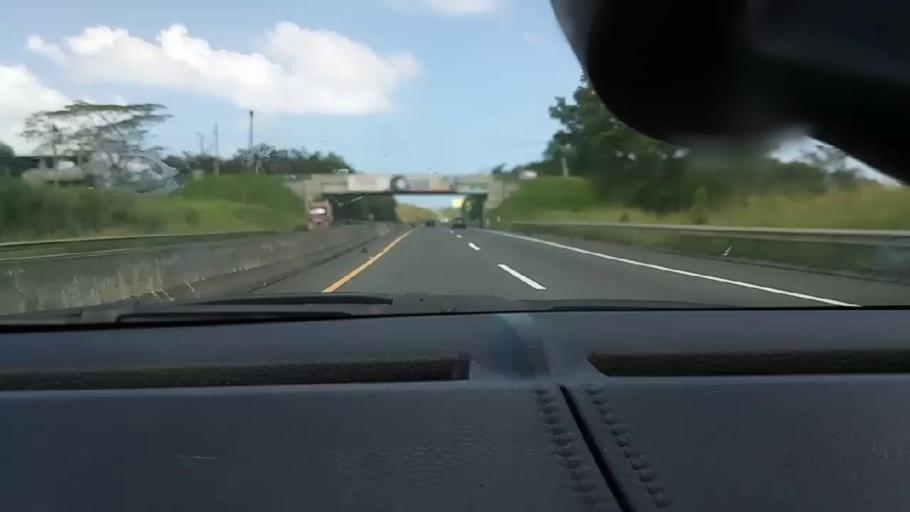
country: PA
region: Colon
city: Las Margaritas
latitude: 9.3300
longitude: -79.8747
